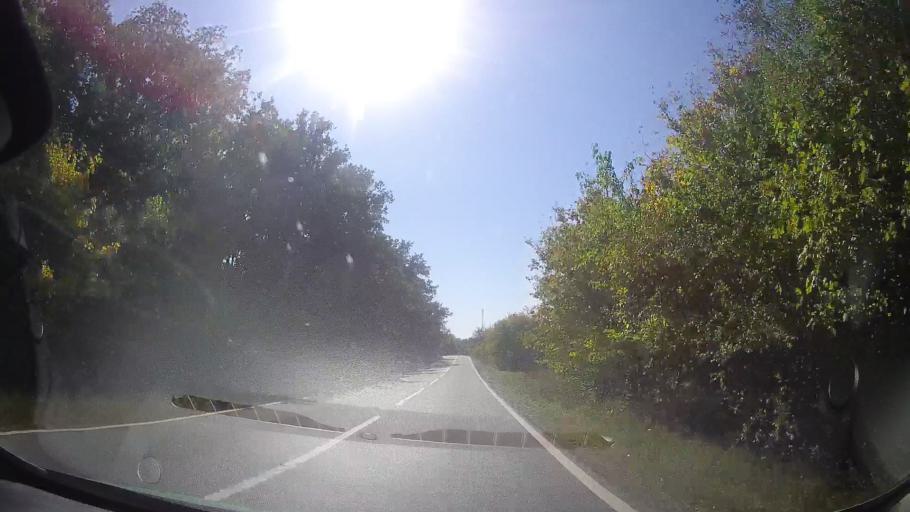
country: RO
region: Timis
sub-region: Municipiul Lugoj
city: Lugoj
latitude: 45.7098
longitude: 21.9663
